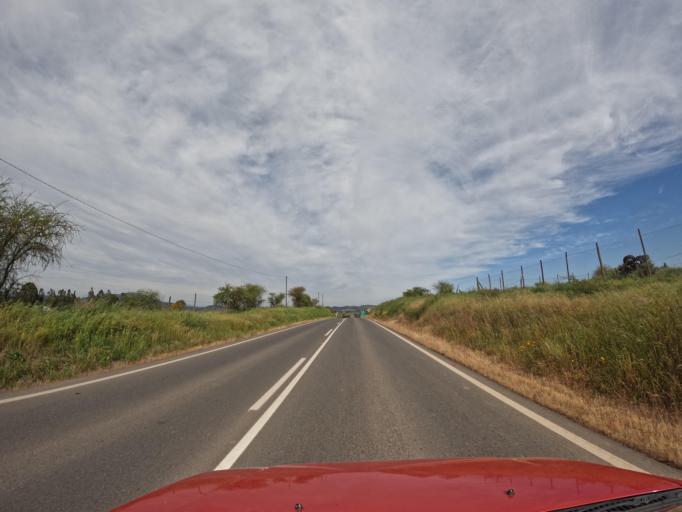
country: CL
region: Maule
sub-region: Provincia de Talca
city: Talca
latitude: -35.3738
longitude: -71.8387
